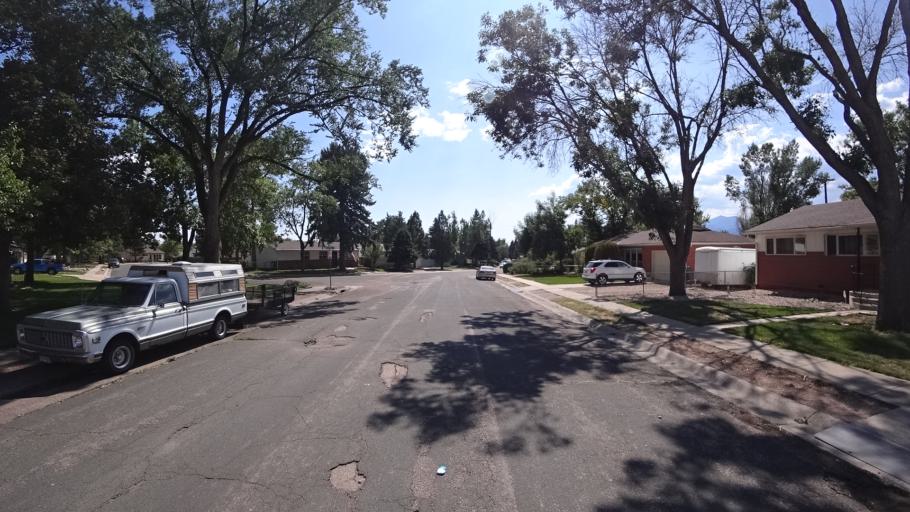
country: US
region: Colorado
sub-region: El Paso County
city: Colorado Springs
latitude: 38.8839
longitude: -104.8082
